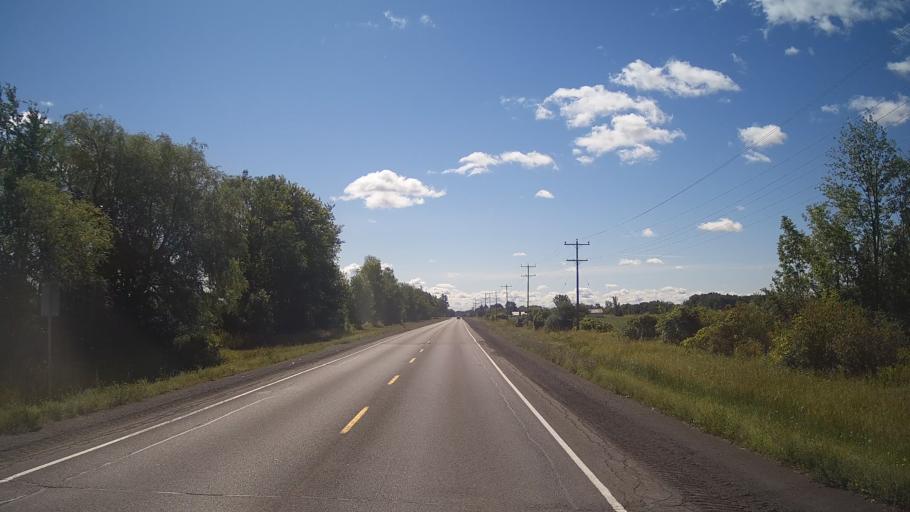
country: US
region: New York
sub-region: St. Lawrence County
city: Norfolk
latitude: 44.9459
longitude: -75.2206
